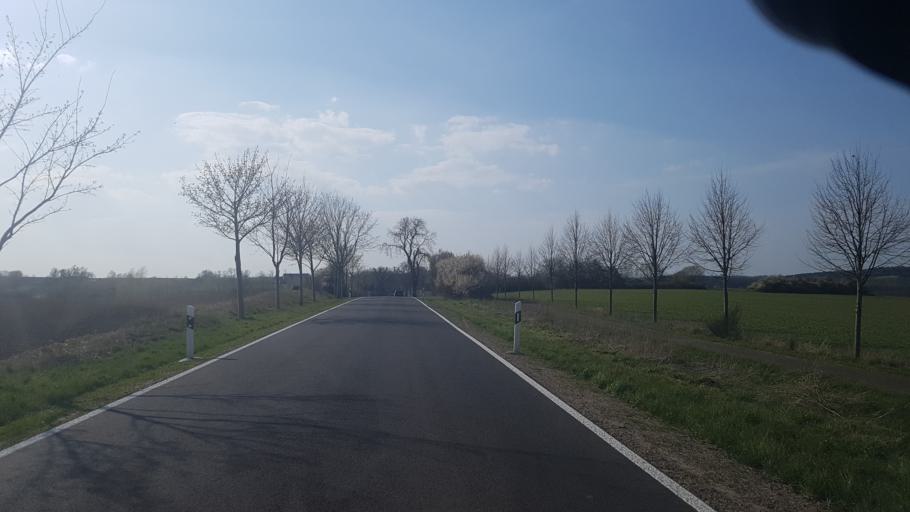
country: DE
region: Brandenburg
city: Gerswalde
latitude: 53.1601
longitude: 13.8262
